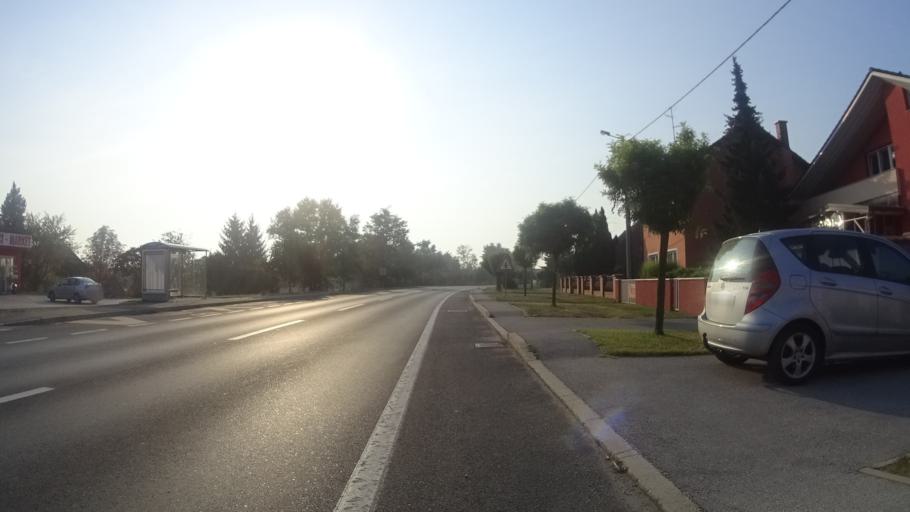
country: HR
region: Varazdinska
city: Sracinec
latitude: 46.3351
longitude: 16.2636
